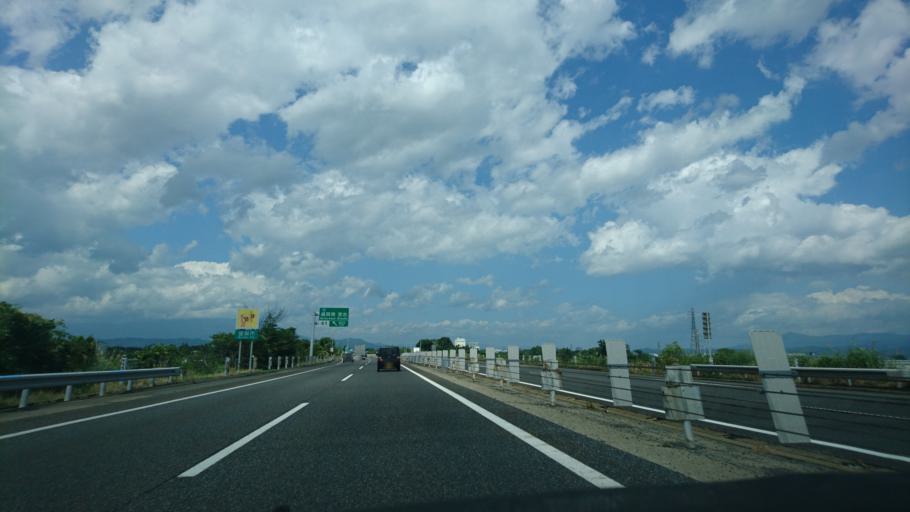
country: JP
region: Iwate
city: Morioka-shi
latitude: 39.6475
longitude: 141.1244
